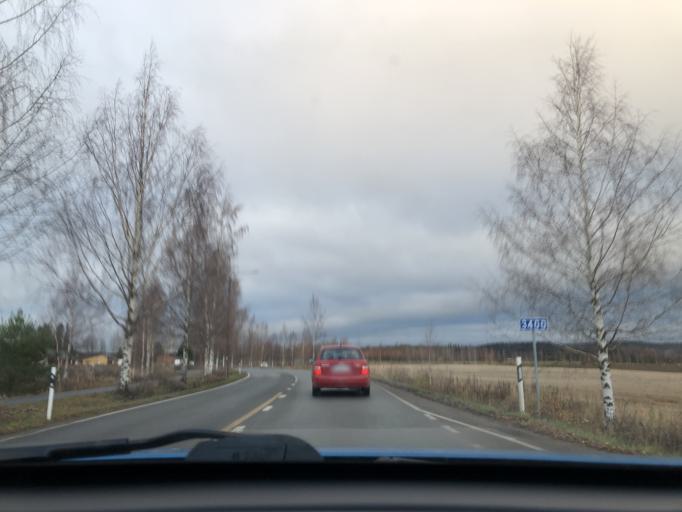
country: FI
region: Pirkanmaa
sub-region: Tampere
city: Kangasala
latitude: 61.4712
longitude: 24.0578
